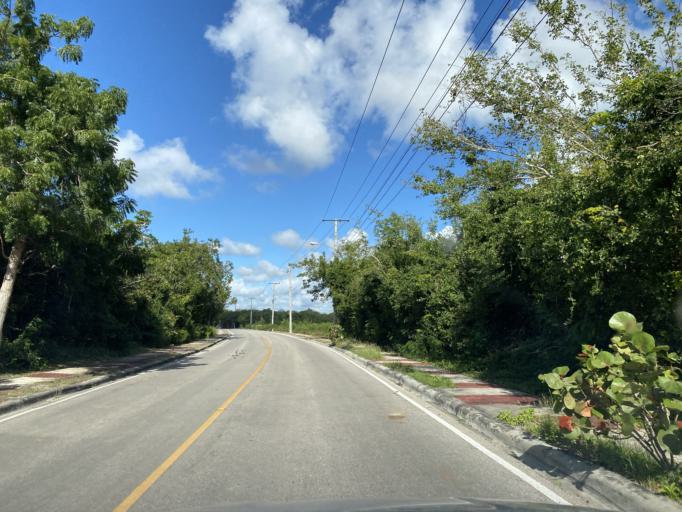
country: DO
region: La Altagracia
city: San Rafael del Yuma
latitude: 18.3417
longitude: -68.8132
